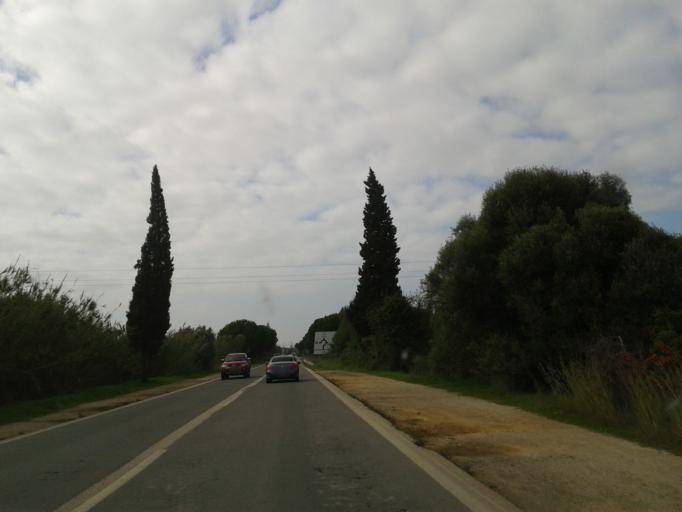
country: PT
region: Faro
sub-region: Vila Real de Santo Antonio
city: Monte Gordo
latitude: 37.1767
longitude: -7.5263
